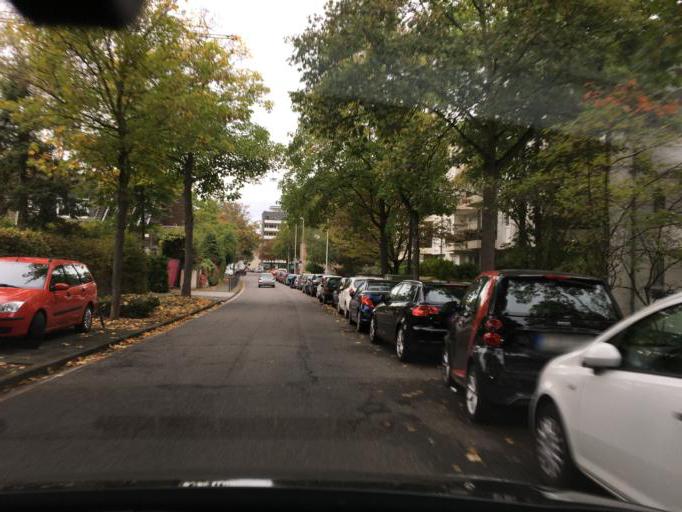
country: DE
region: North Rhine-Westphalia
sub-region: Regierungsbezirk Koln
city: Bonn
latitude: 50.7358
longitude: 7.1208
